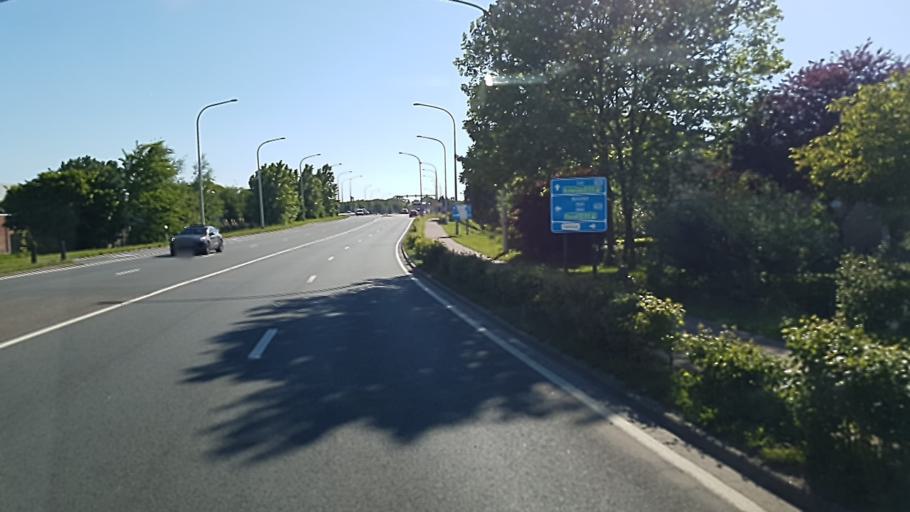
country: BE
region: Flanders
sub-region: Provincie Antwerpen
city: Herentals
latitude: 51.1728
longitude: 4.8490
